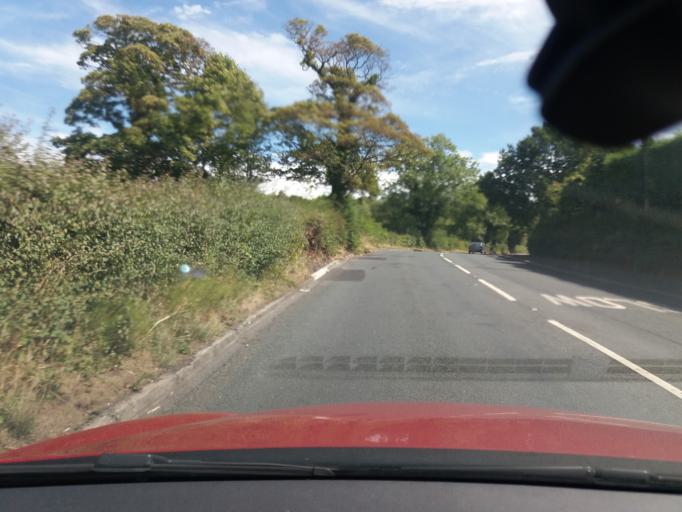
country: GB
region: England
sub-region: Lancashire
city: Euxton
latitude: 53.6615
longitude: -2.7061
